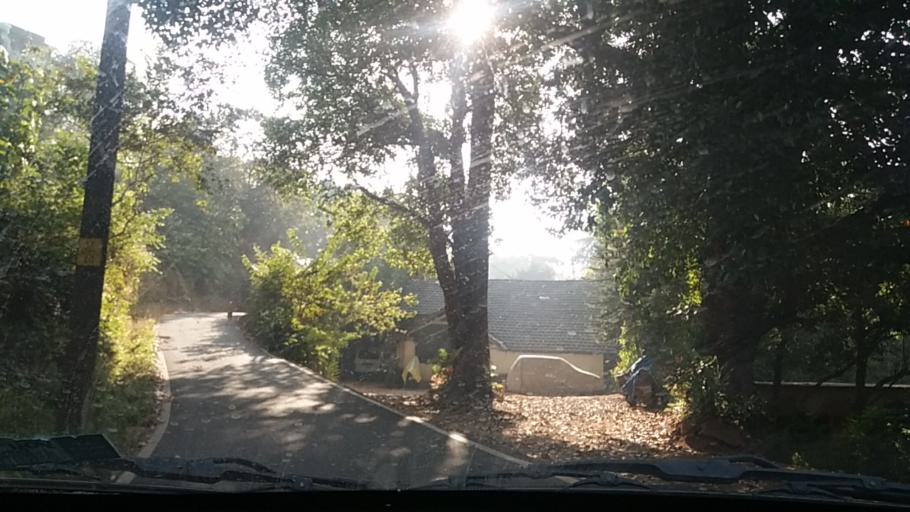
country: IN
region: Goa
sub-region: South Goa
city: Curchorem
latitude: 15.2637
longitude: 74.1138
